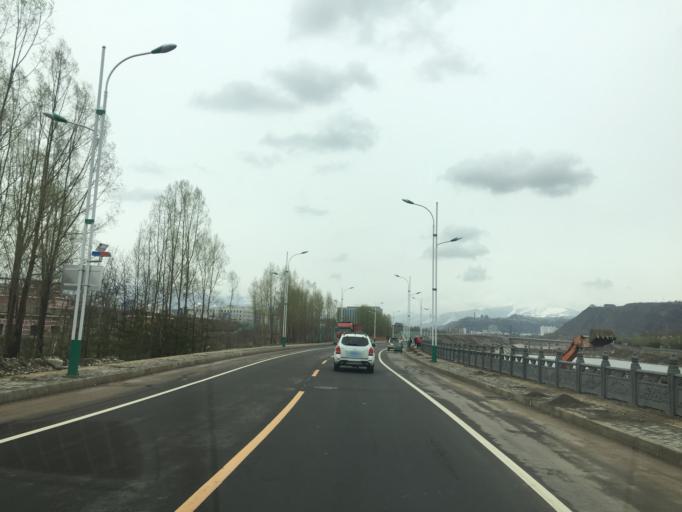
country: CN
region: Gansu Sheng
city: Hanji
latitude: 35.4931
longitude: 103.0716
